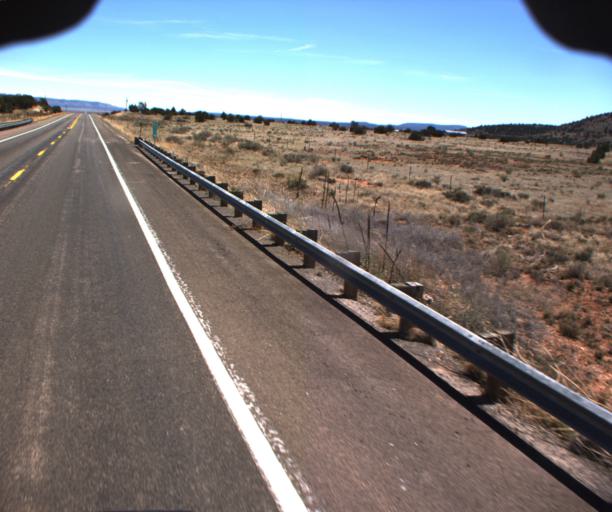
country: US
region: Arizona
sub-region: Mohave County
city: Peach Springs
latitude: 35.5031
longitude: -113.1766
